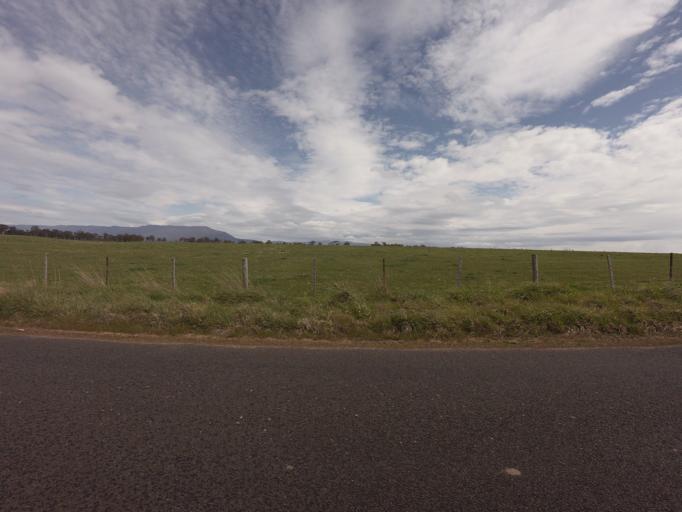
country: AU
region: Tasmania
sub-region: Northern Midlands
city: Evandale
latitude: -41.7922
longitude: 147.2497
